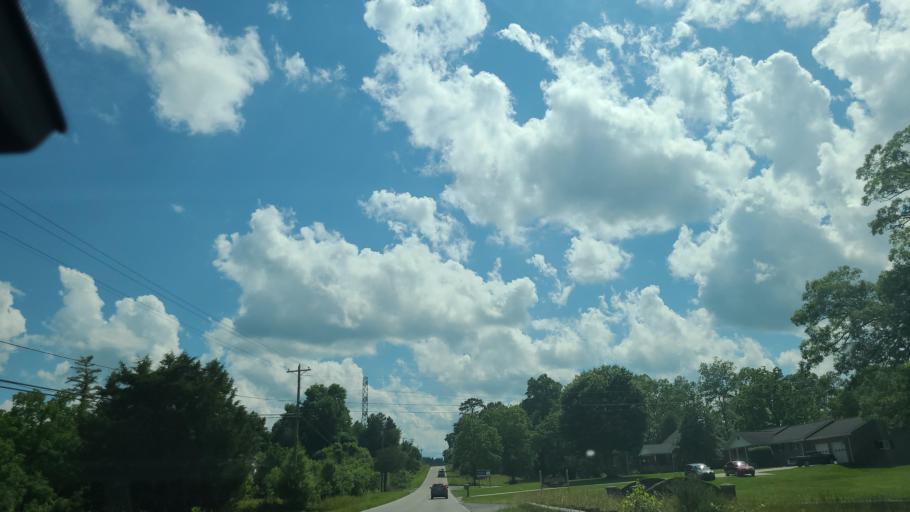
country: US
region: Kentucky
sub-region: Whitley County
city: Corbin
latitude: 36.8883
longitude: -84.1914
